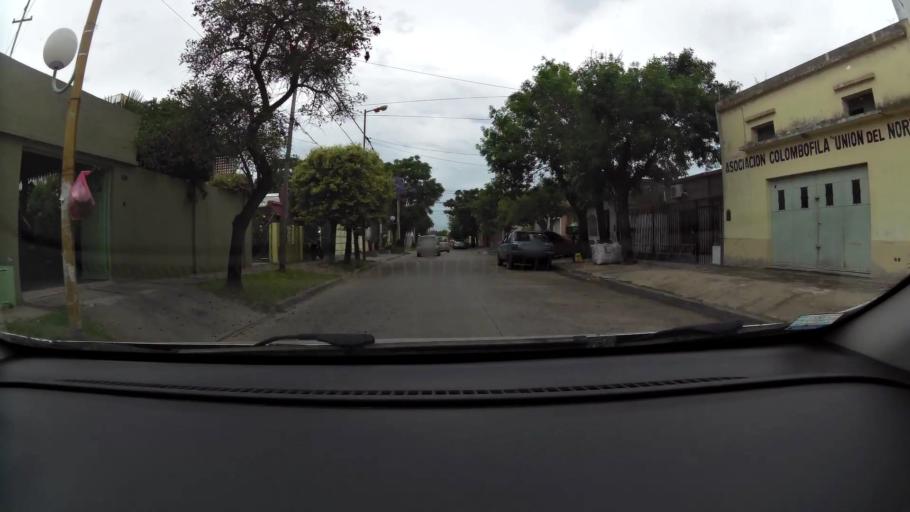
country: AR
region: Buenos Aires
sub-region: Partido de Zarate
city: Zarate
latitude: -34.0882
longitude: -59.0345
